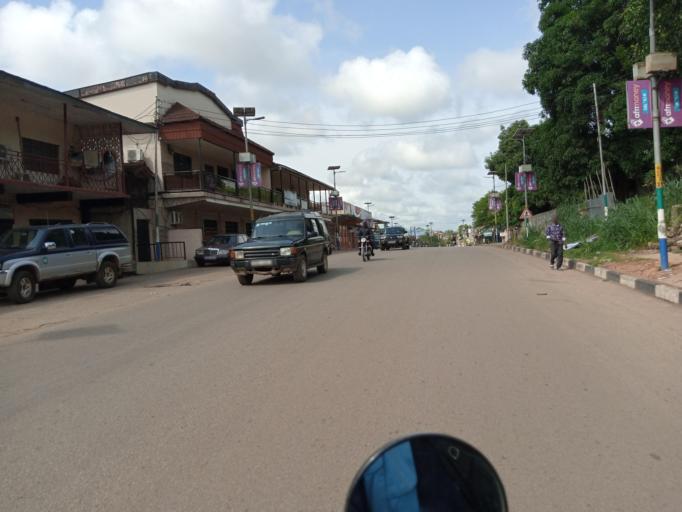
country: SL
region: Southern Province
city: Bo
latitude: 7.9632
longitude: -11.7399
